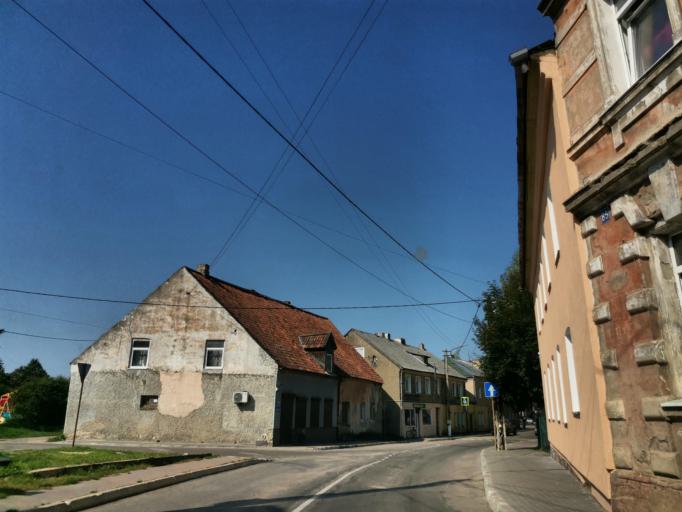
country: RU
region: Kaliningrad
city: Neman
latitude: 55.0349
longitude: 22.0359
